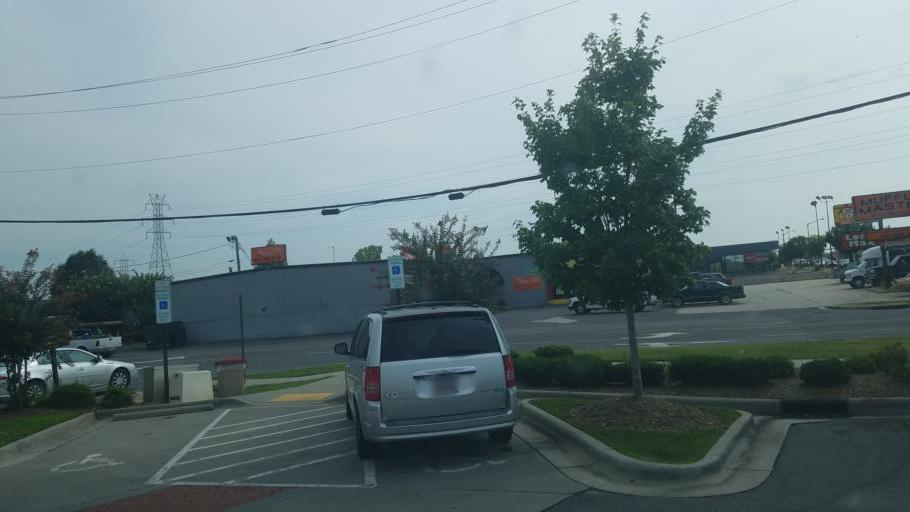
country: US
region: South Carolina
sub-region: York County
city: India Hook
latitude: 34.9722
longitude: -80.9881
